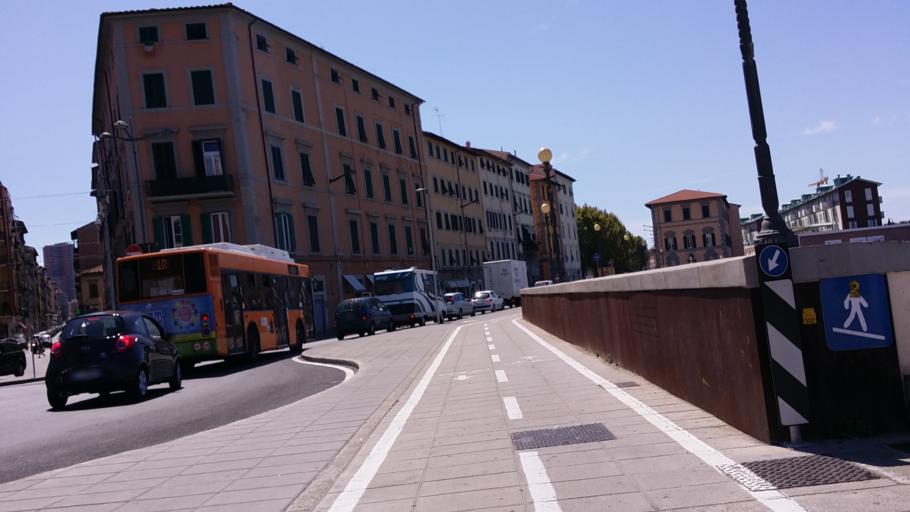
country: IT
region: Tuscany
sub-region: Provincia di Livorno
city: Livorno
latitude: 43.5467
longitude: 10.3044
